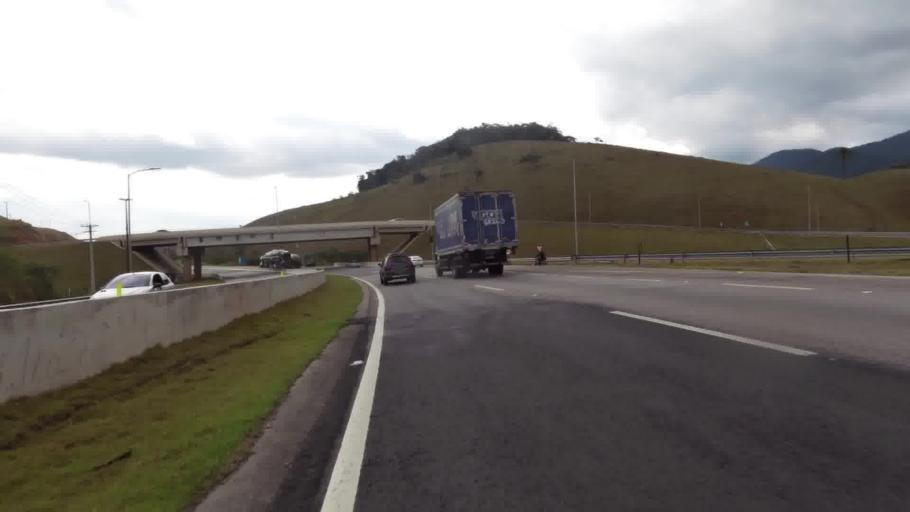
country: BR
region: Rio de Janeiro
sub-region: Casimiro De Abreu
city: Casimiro de Abreu
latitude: -22.4649
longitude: -42.0699
